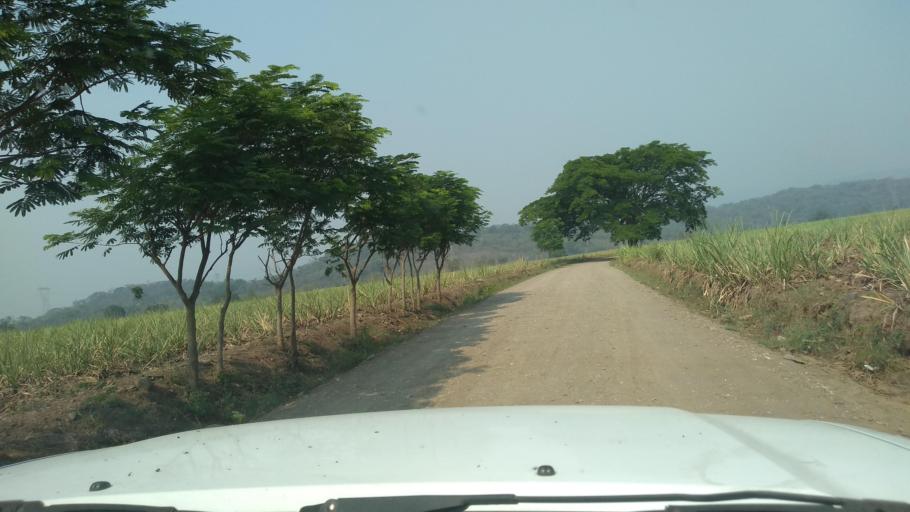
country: MX
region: Oaxaca
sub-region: Cosolapa
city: Cosolapa
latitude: 18.6187
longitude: -96.6282
